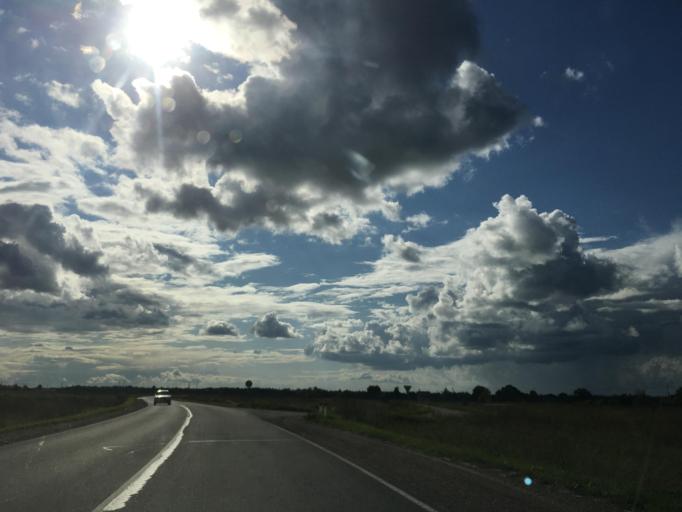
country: RU
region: Pskov
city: Izborsk
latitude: 57.8381
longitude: 28.0658
